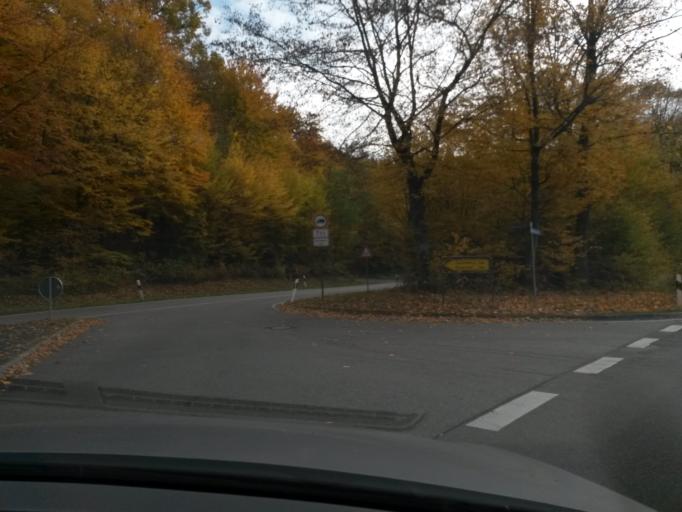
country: DE
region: Baden-Wuerttemberg
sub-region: Karlsruhe Region
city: Ettlingen
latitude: 48.9141
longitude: 8.4584
